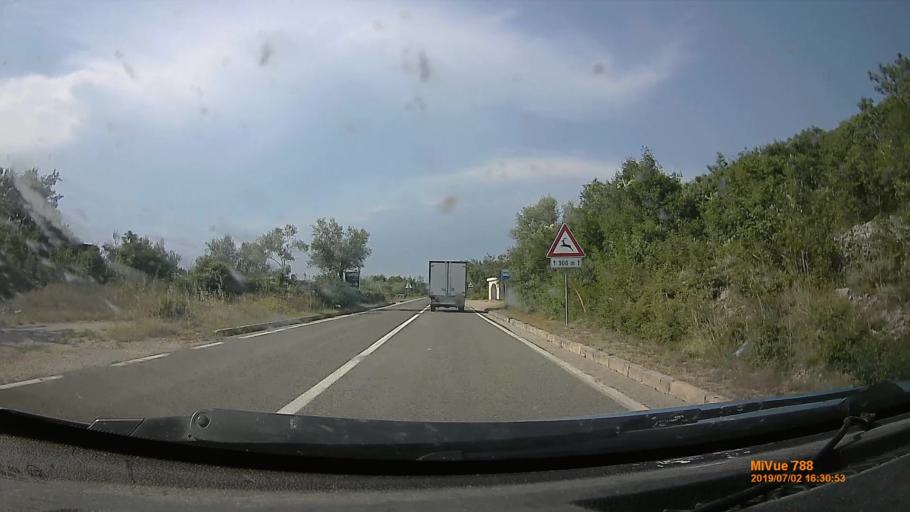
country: HR
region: Primorsko-Goranska
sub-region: Grad Krk
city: Krk
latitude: 45.0476
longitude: 14.4889
